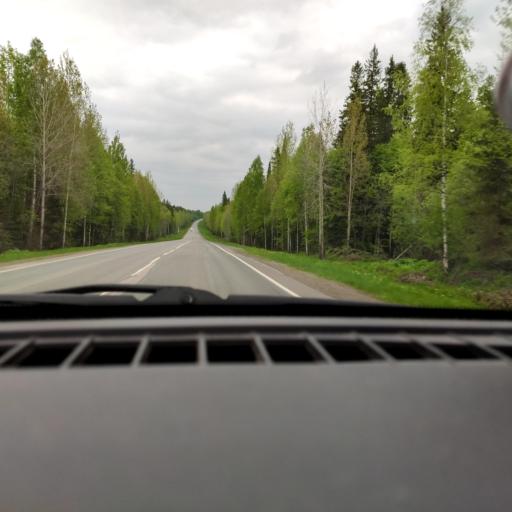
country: RU
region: Perm
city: Perm
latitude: 58.2299
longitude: 56.1623
